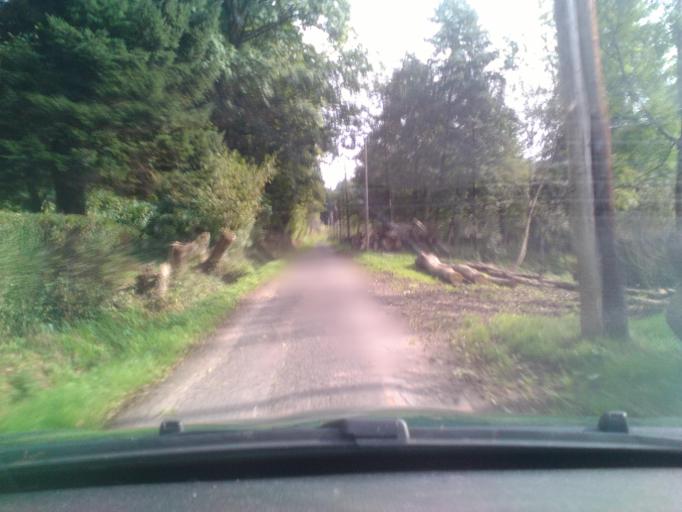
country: FR
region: Lorraine
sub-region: Departement des Vosges
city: Taintrux
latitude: 48.2334
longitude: 6.8637
